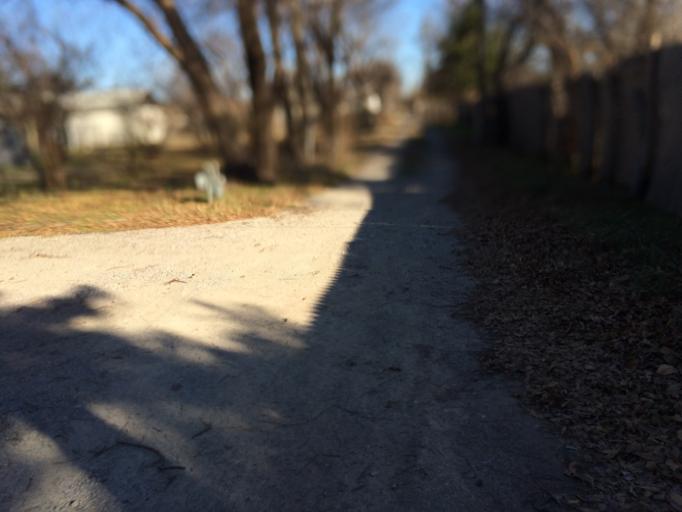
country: US
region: Oklahoma
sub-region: Cleveland County
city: Norman
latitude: 35.2311
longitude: -97.4491
